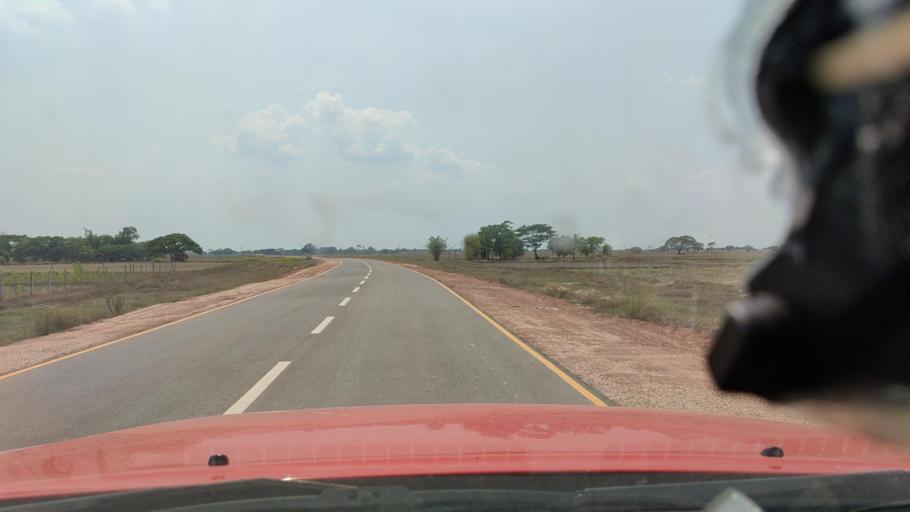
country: MM
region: Bago
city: Thanatpin
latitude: 17.0455
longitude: 96.3666
